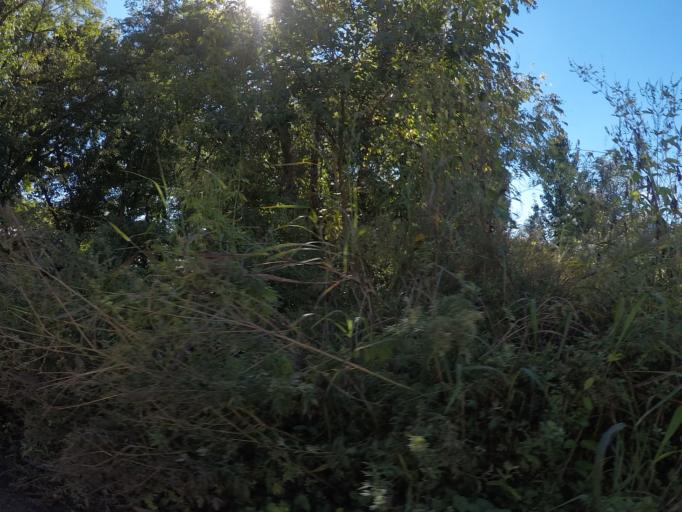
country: US
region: Ohio
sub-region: Lawrence County
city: Burlington
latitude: 38.4000
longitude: -82.5200
